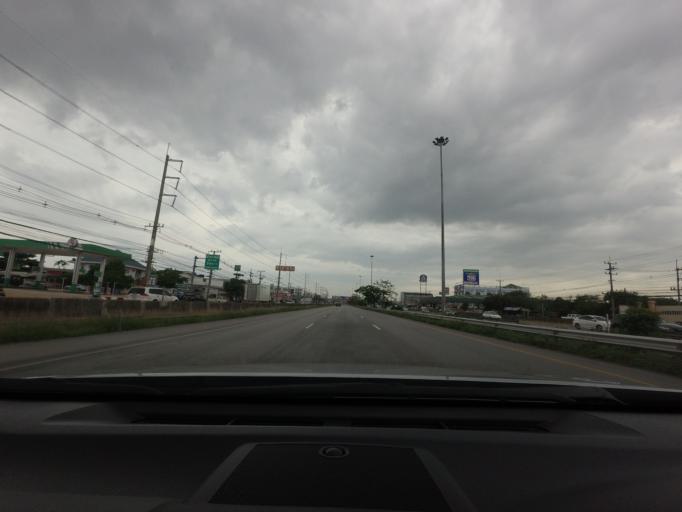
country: TH
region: Samut Sakhon
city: Samut Sakhon
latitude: 13.5432
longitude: 100.2442
